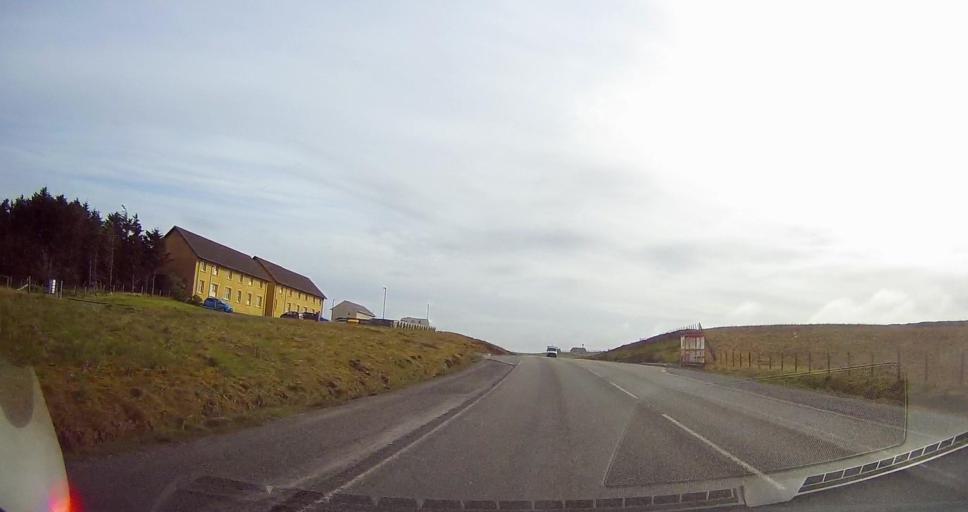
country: GB
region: Scotland
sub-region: Shetland Islands
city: Lerwick
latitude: 60.1411
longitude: -1.1856
